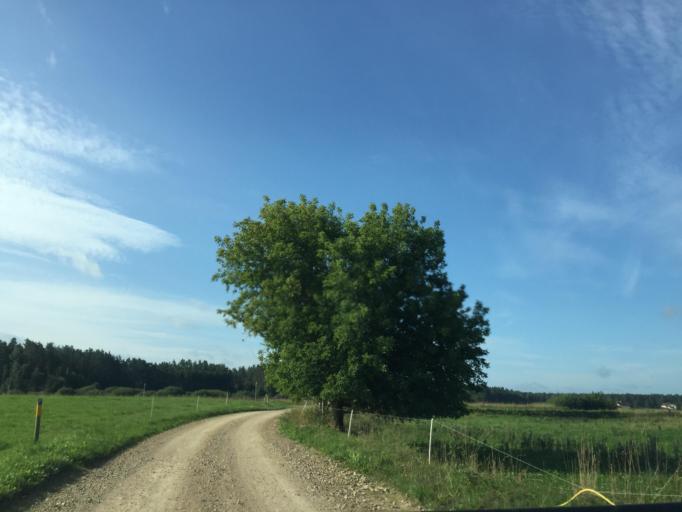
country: LV
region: Garkalne
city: Garkalne
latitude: 57.0663
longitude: 24.3881
